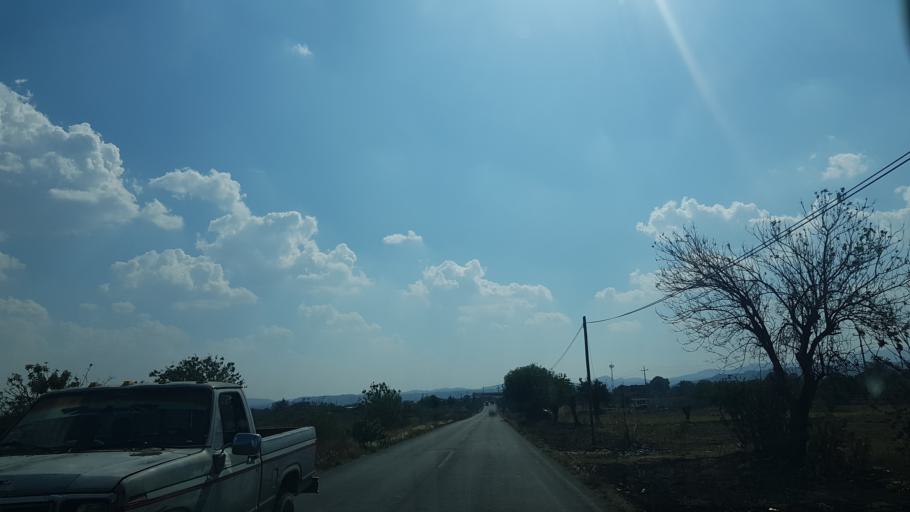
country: MX
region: Puebla
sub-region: Atlixco
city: Colonia Agricola de Ocotepec (Colonia San Jose)
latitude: 18.8962
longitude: -98.5066
